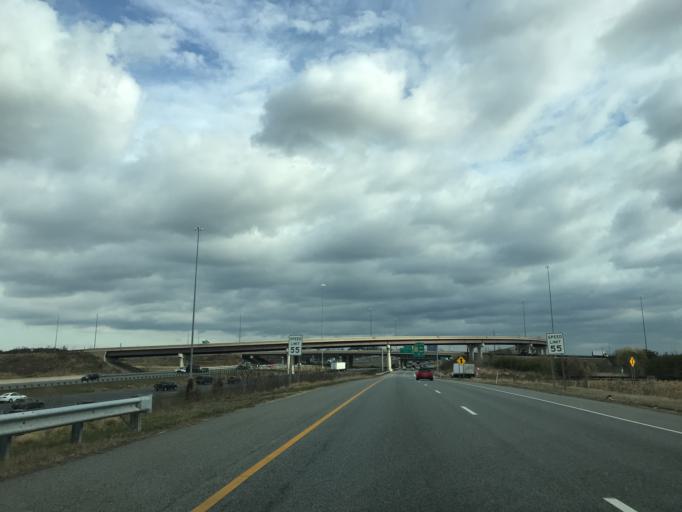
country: US
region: Maryland
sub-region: Prince George's County
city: Calverton
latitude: 39.0702
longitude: -76.9068
